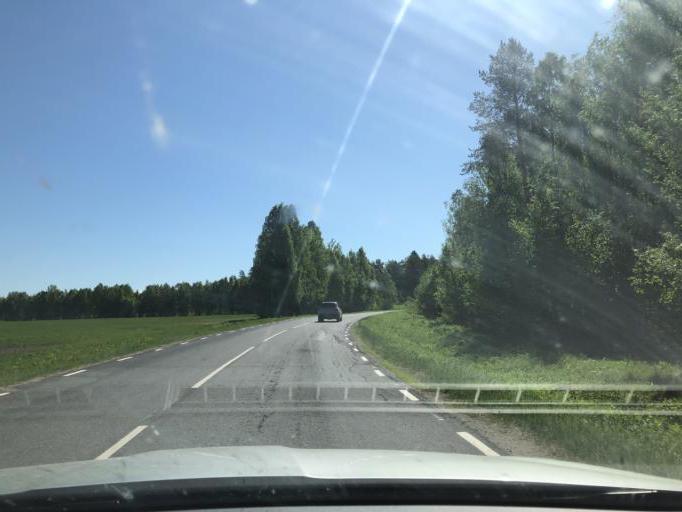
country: SE
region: Norrbotten
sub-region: Lulea Kommun
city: Gammelstad
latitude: 65.6594
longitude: 21.9915
